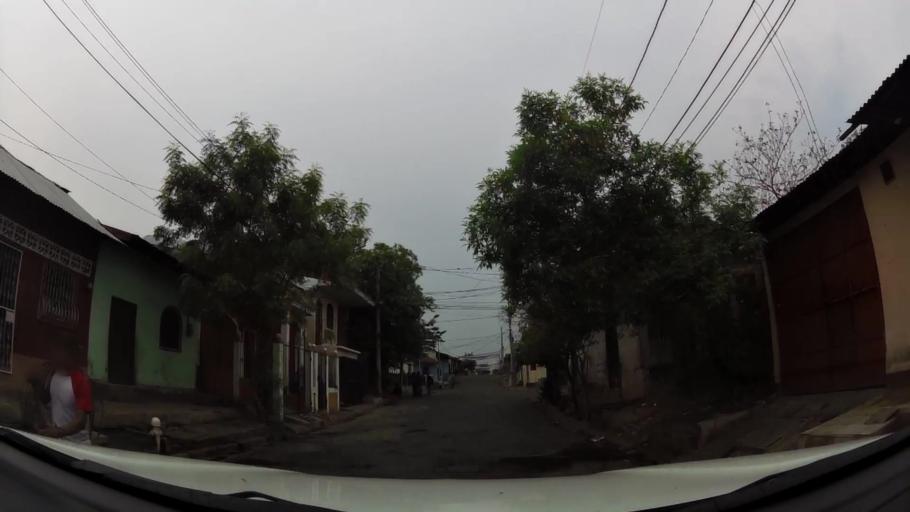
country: NI
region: Leon
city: Leon
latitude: 12.4283
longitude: -86.8800
